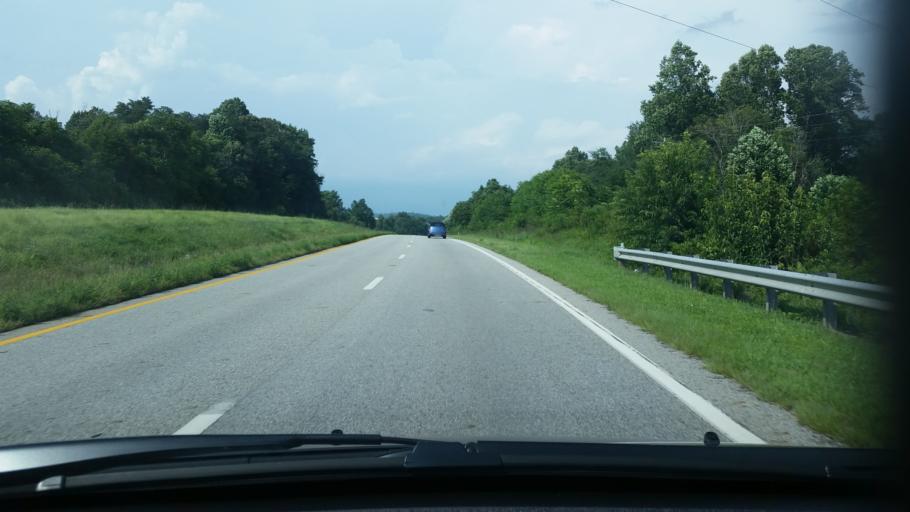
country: US
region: Virginia
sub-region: Nelson County
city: Lovingston
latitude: 37.7227
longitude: -78.9002
